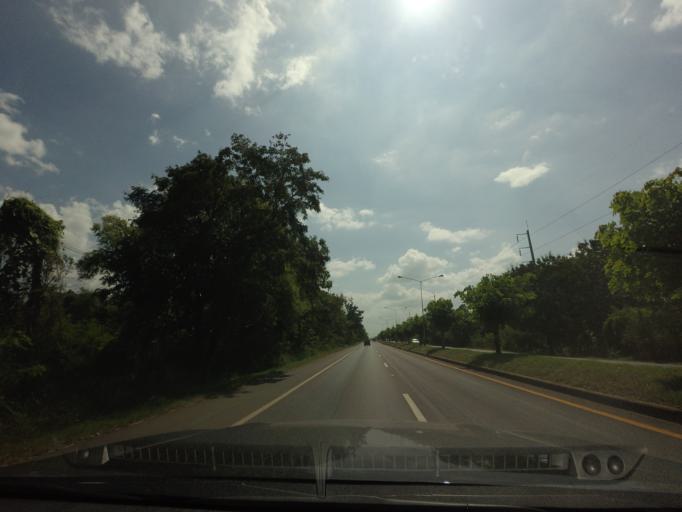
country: TH
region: Phetchabun
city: Nong Phai
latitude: 15.8939
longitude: 101.0250
